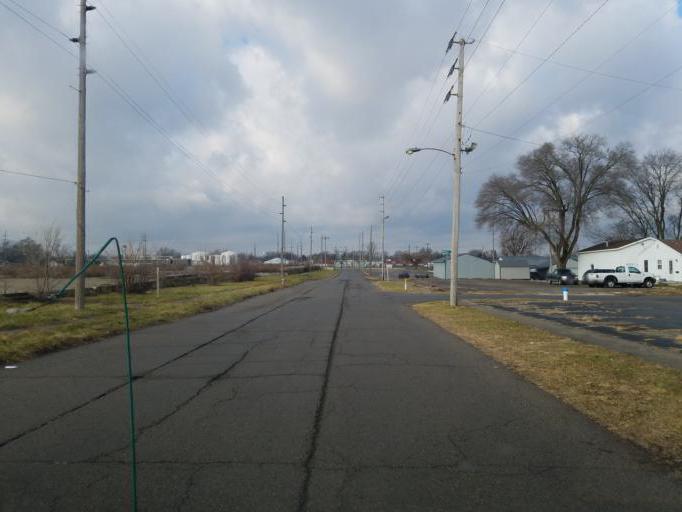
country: US
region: Ohio
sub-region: Marion County
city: Marion
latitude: 40.5963
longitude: -83.1345
